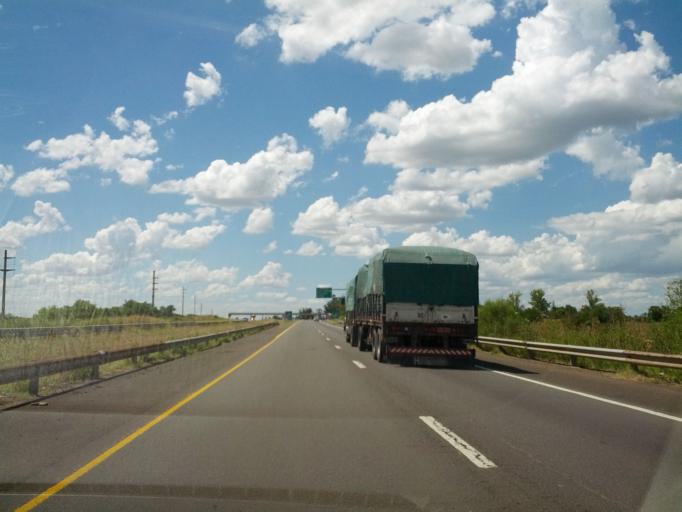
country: AR
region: Entre Rios
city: Concepcion del Uruguay
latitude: -32.4111
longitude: -58.2796
